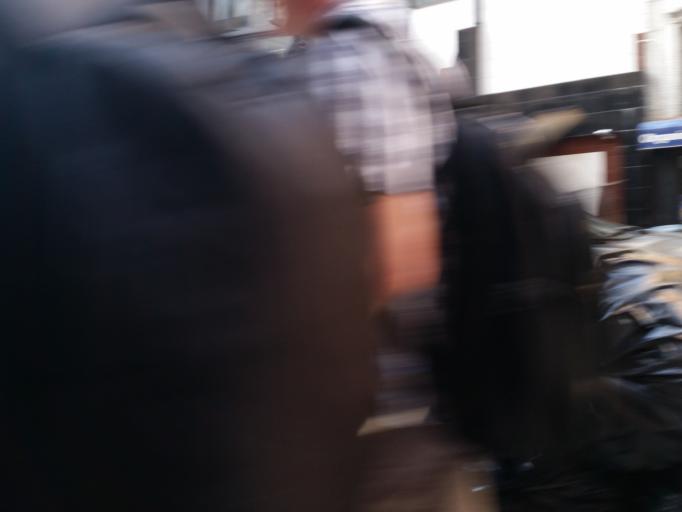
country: US
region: New York
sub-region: Queens County
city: Long Island City
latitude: 40.7521
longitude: -73.9700
